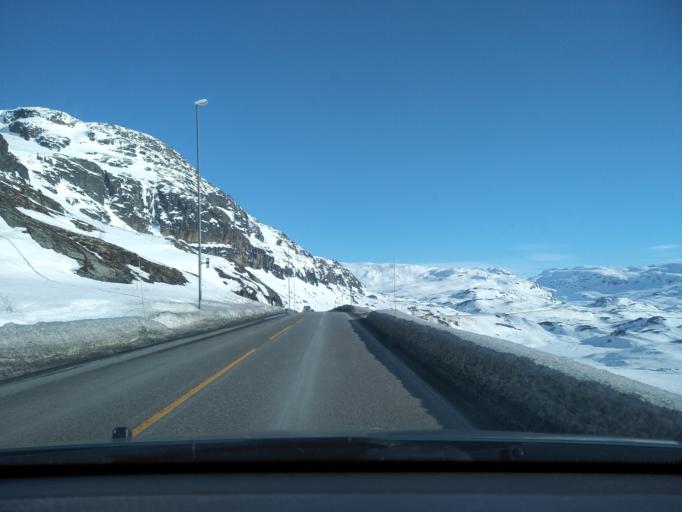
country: NO
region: Hordaland
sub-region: Odda
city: Odda
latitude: 59.8491
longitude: 6.9545
